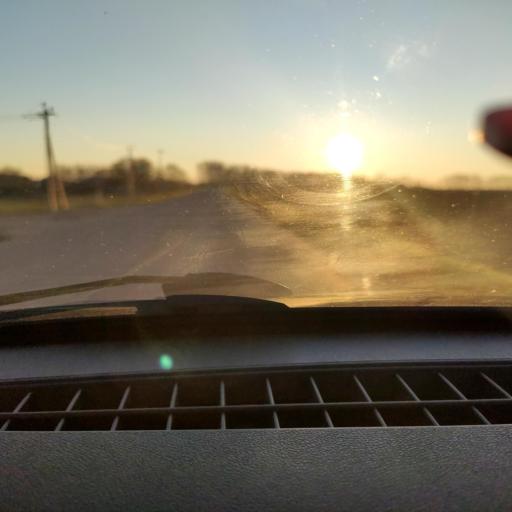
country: RU
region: Bashkortostan
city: Avdon
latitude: 54.5508
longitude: 55.6609
